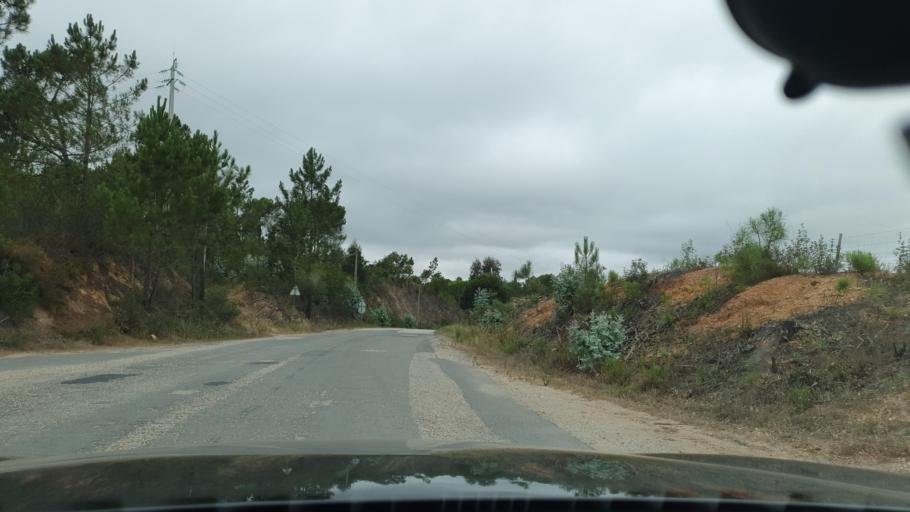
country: PT
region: Beja
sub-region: Odemira
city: Sao Teotonio
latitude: 37.5068
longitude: -8.6955
